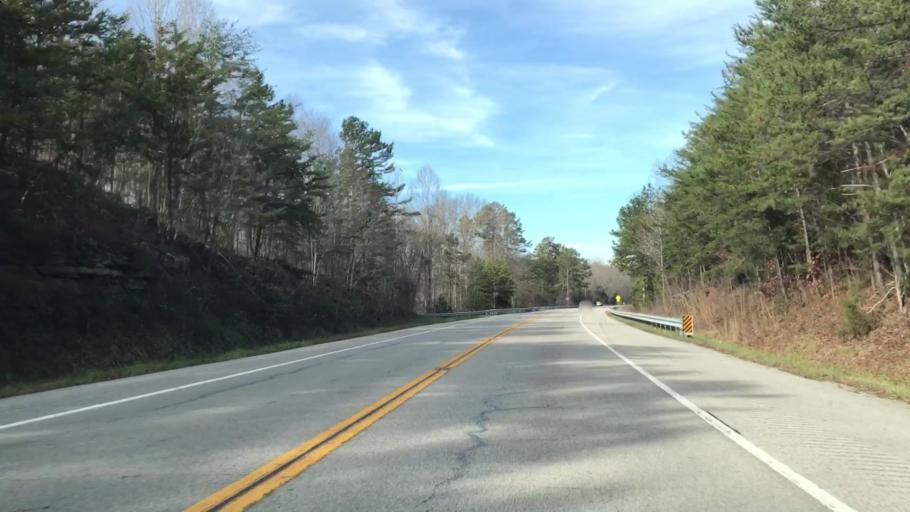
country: US
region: Kentucky
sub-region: McCreary County
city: Whitley City
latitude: 36.9134
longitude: -84.5142
